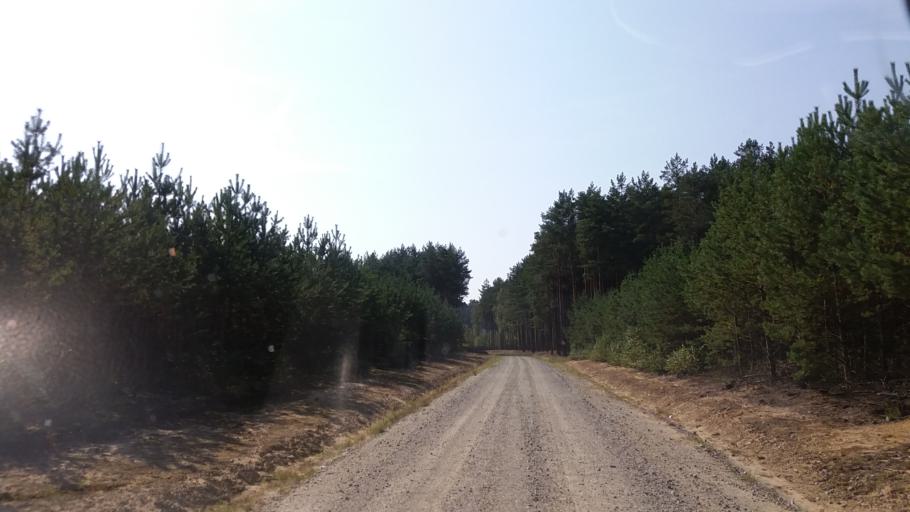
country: PL
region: West Pomeranian Voivodeship
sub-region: Powiat drawski
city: Kalisz Pomorski
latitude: 53.1892
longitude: 15.9589
